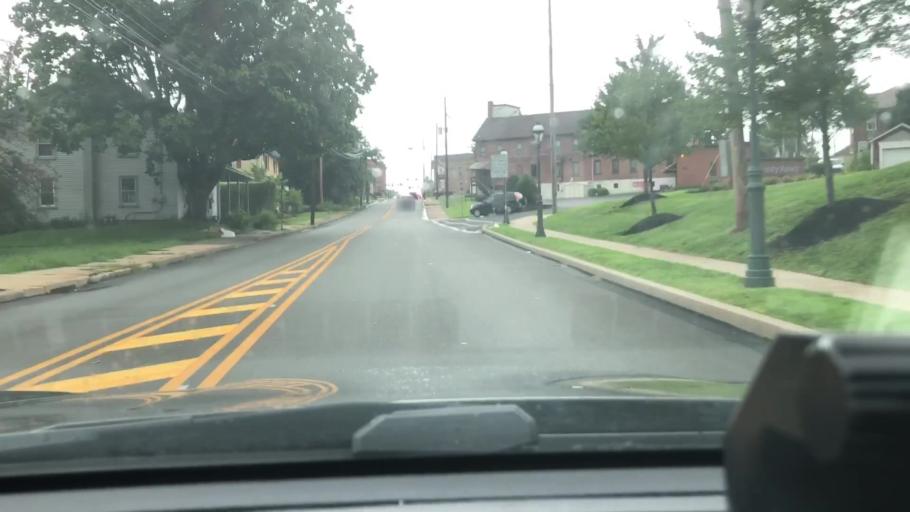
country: US
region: Pennsylvania
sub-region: Montgomery County
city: Pennsburg
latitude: 40.3962
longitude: -75.4991
